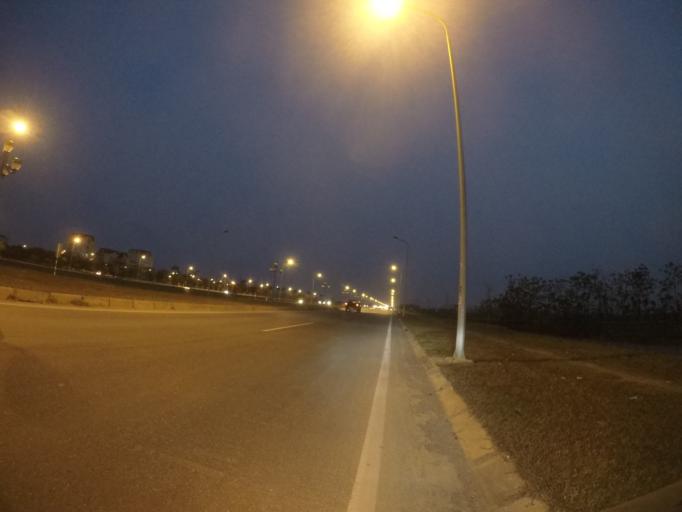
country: VN
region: Ha Noi
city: Me Linh
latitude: 21.1819
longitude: 105.7167
